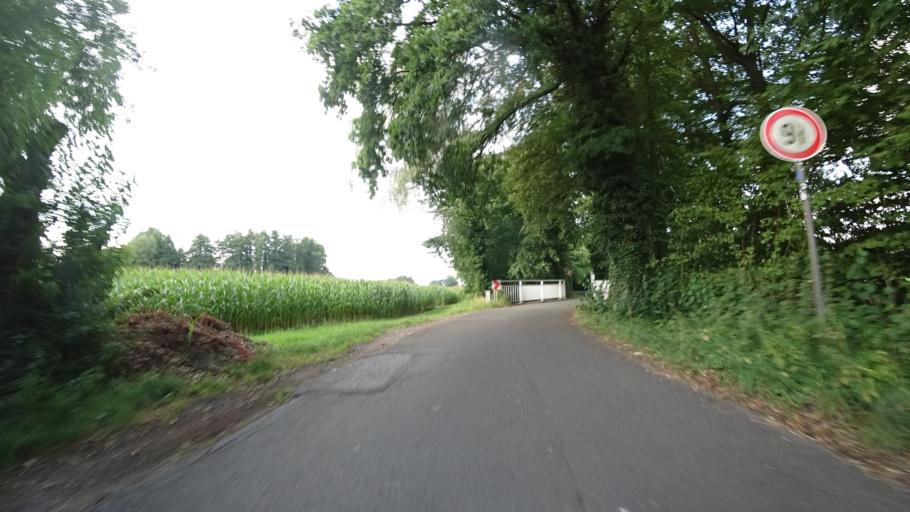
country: DE
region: North Rhine-Westphalia
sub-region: Regierungsbezirk Detmold
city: Guetersloh
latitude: 51.9471
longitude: 8.4155
